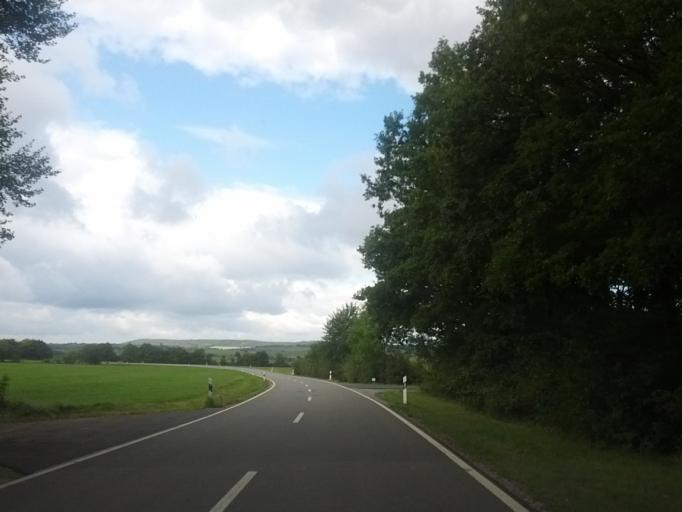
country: DE
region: Hesse
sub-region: Regierungsbezirk Kassel
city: Weissenborn
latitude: 51.0636
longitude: 10.1018
